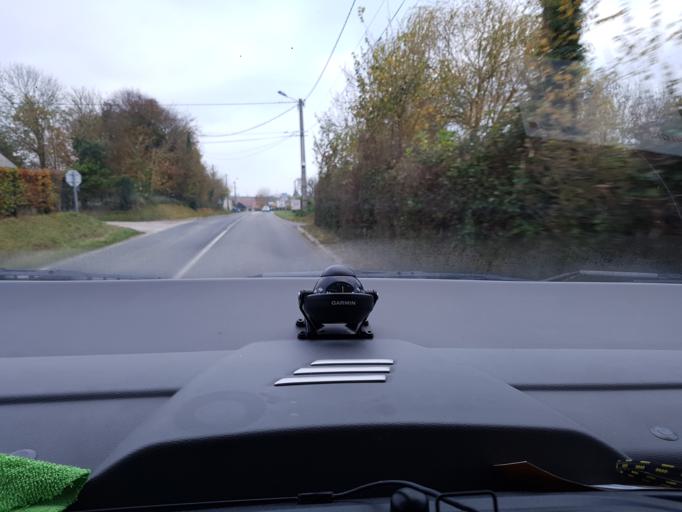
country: FR
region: Picardie
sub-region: Departement de la Somme
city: Ault
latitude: 50.1262
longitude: 1.4908
